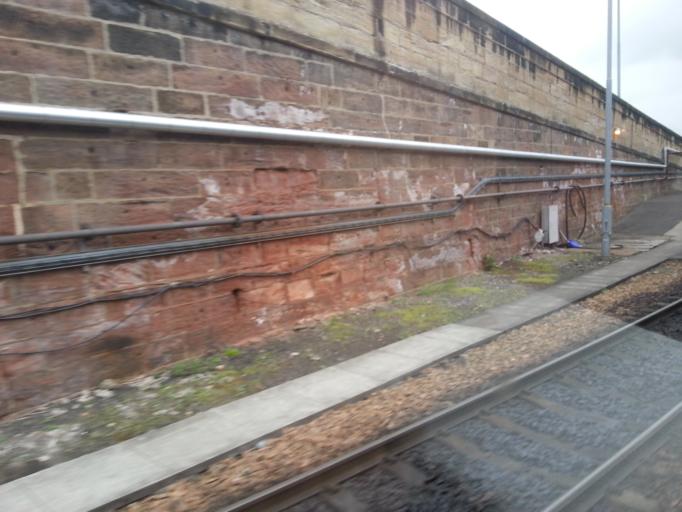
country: GB
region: Scotland
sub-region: Perth and Kinross
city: Perth
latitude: 56.3944
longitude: -3.4414
